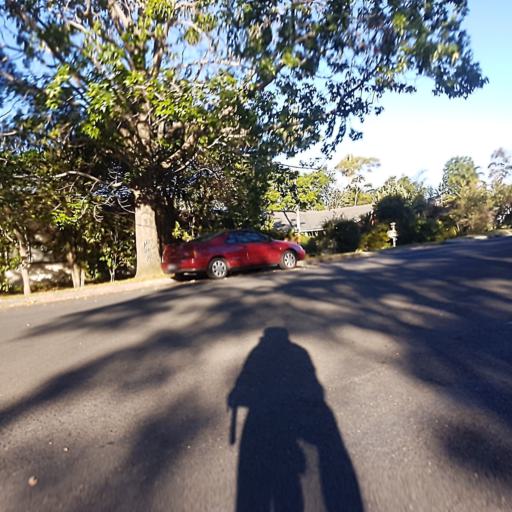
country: AU
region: New South Wales
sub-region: Warringah
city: Forestville
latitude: -33.7579
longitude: 151.2123
